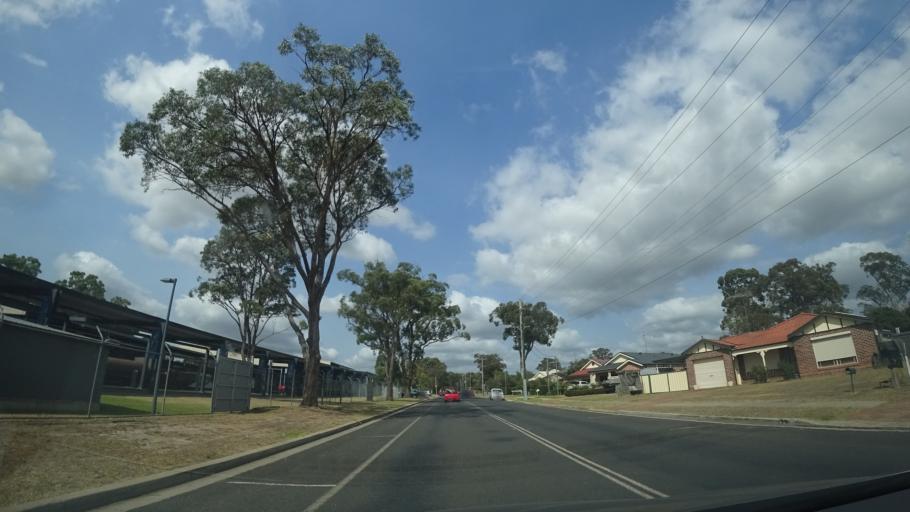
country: AU
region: New South Wales
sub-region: Wollondilly
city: Picton
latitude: -34.2064
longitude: 150.5691
